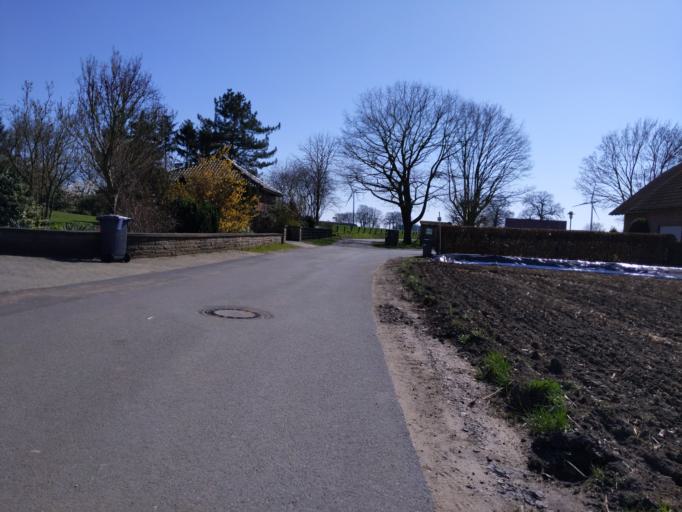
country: DE
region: North Rhine-Westphalia
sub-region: Regierungsbezirk Dusseldorf
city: Schermbeck
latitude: 51.6946
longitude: 6.9043
